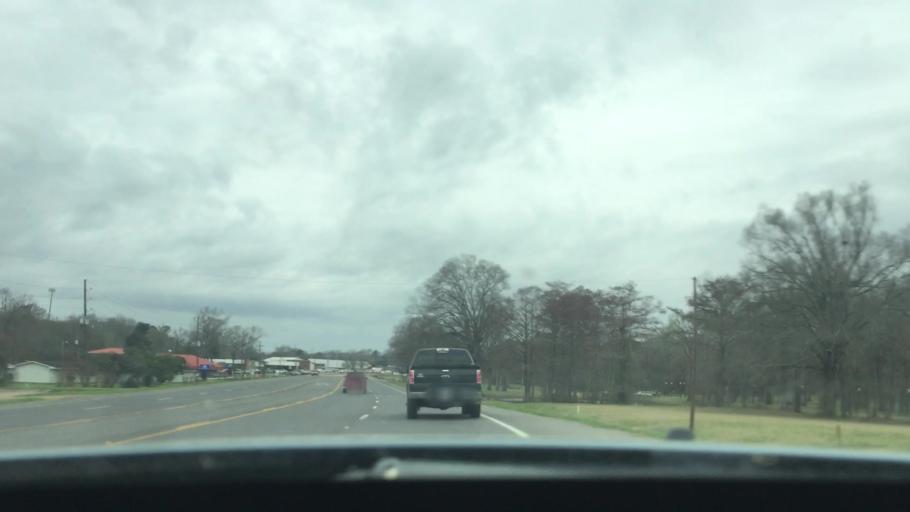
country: US
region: Louisiana
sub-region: Franklin Parish
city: Winnsboro
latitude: 32.1533
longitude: -91.7086
